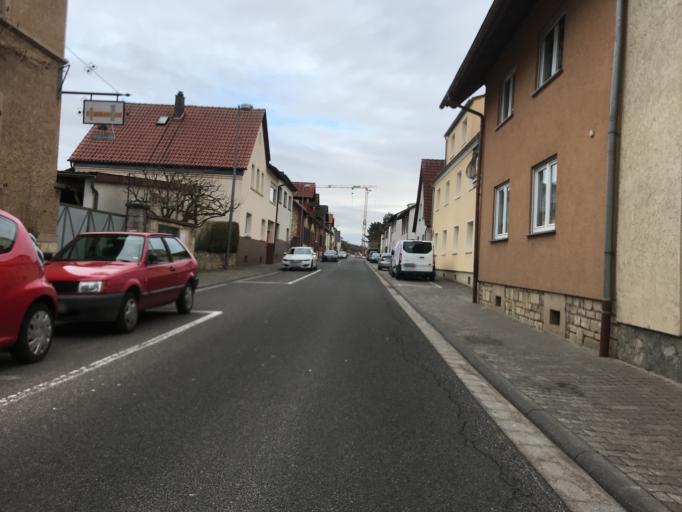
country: DE
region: Rheinland-Pfalz
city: Ingelheim am Rhein
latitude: 49.9600
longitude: 8.0653
